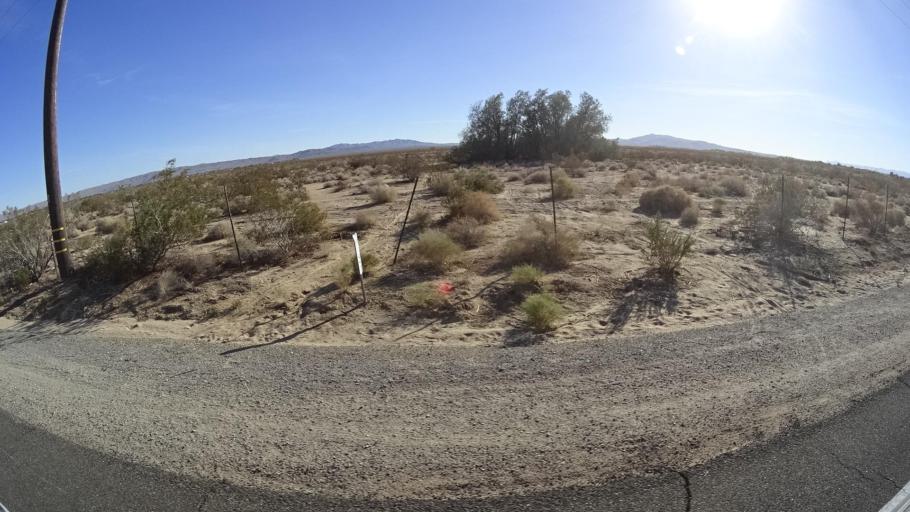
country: US
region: California
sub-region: Kern County
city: China Lake Acres
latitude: 35.6518
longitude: -117.7343
